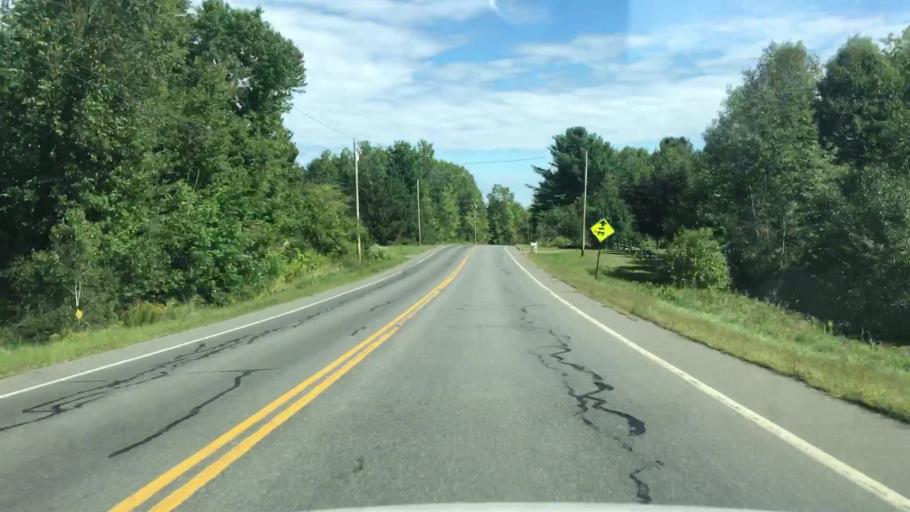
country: US
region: Maine
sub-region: Penobscot County
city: Garland
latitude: 45.0868
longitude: -69.2250
